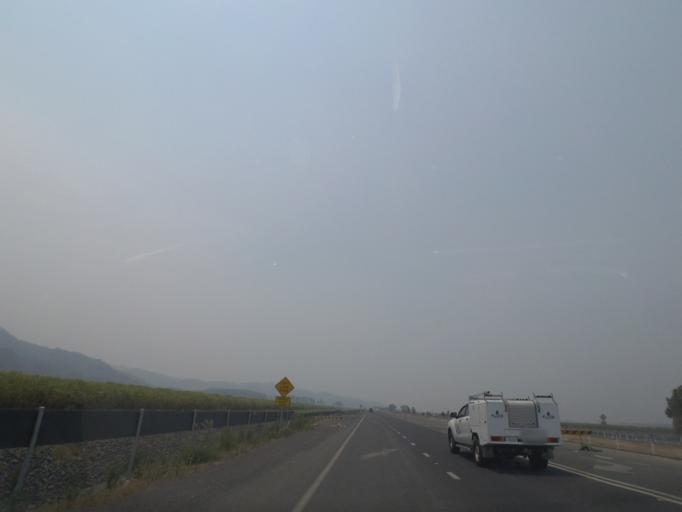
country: AU
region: New South Wales
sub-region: Ballina
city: Ballina
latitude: -28.9005
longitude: 153.4800
